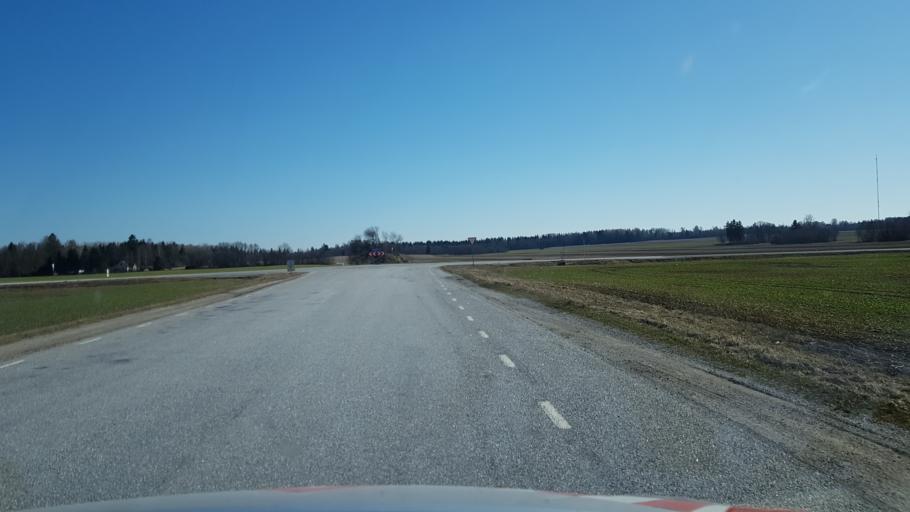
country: EE
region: Jaervamaa
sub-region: Koeru vald
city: Koeru
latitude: 59.0066
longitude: 26.0899
